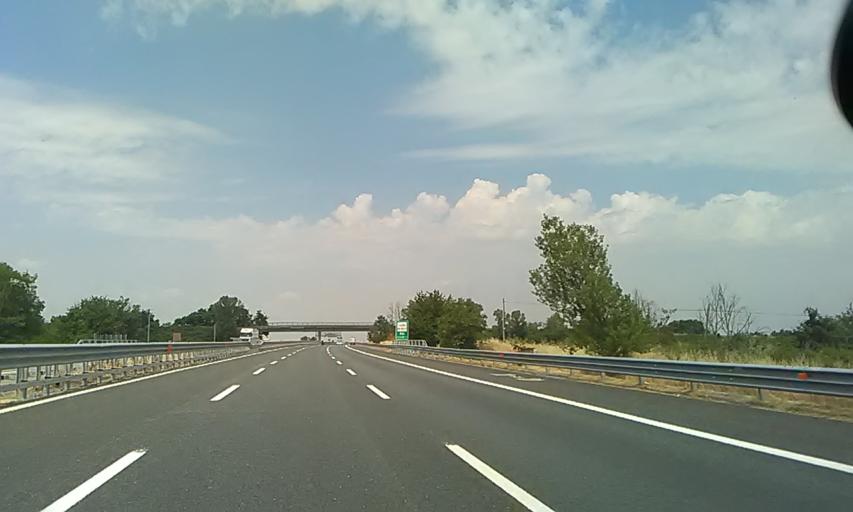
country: IT
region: Piedmont
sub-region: Provincia di Alessandria
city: Predosa
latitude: 44.7680
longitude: 8.6329
